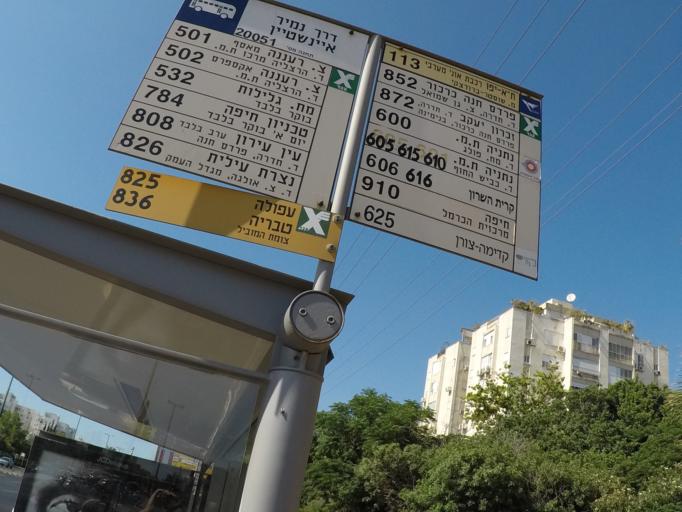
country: IL
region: Tel Aviv
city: Tel Aviv
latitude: 32.1131
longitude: 34.7928
